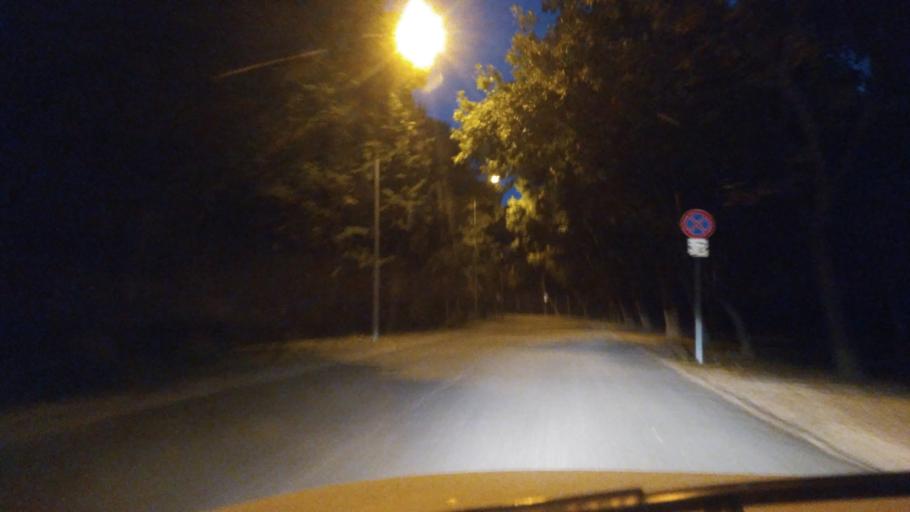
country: HU
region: Budapest
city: Budapest III. keruelet
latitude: 47.5538
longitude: 19.0575
